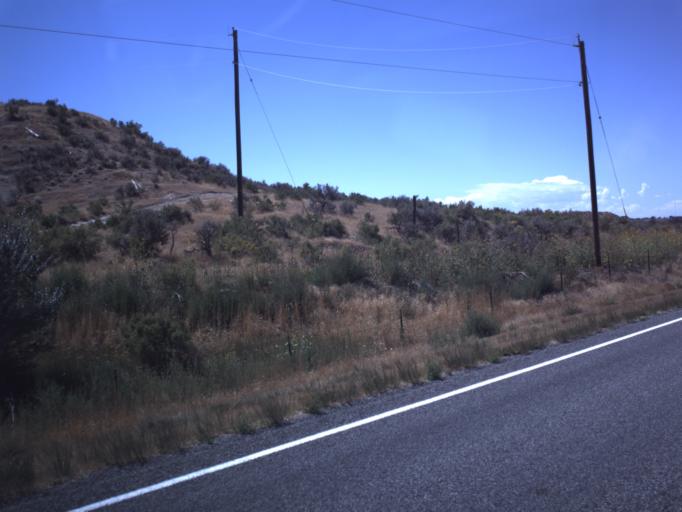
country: US
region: Utah
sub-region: Millard County
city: Delta
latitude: 39.5334
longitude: -112.3132
